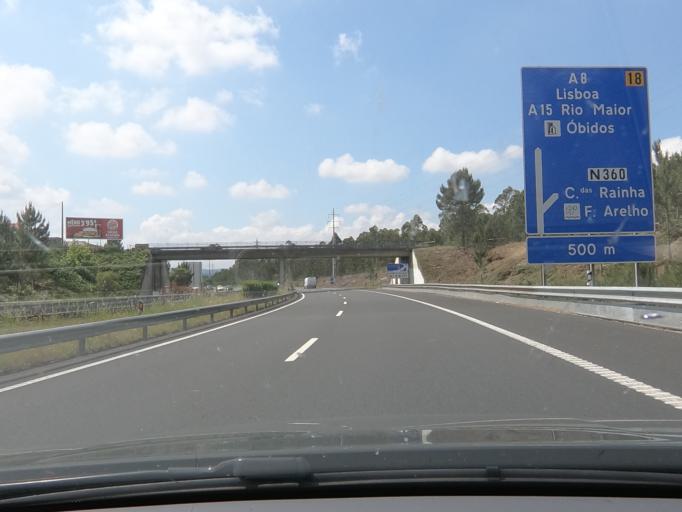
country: PT
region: Leiria
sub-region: Caldas da Rainha
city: Caldas da Rainha
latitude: 39.4140
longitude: -9.1559
